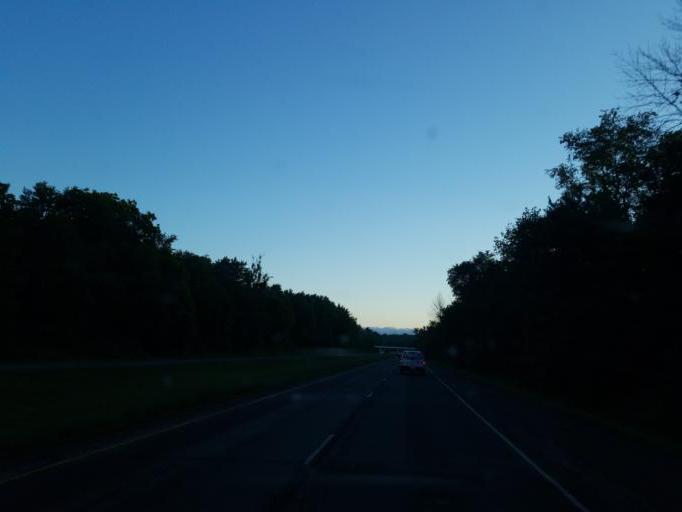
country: US
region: Ohio
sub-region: Summit County
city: Norton
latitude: 41.0207
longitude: -81.6653
